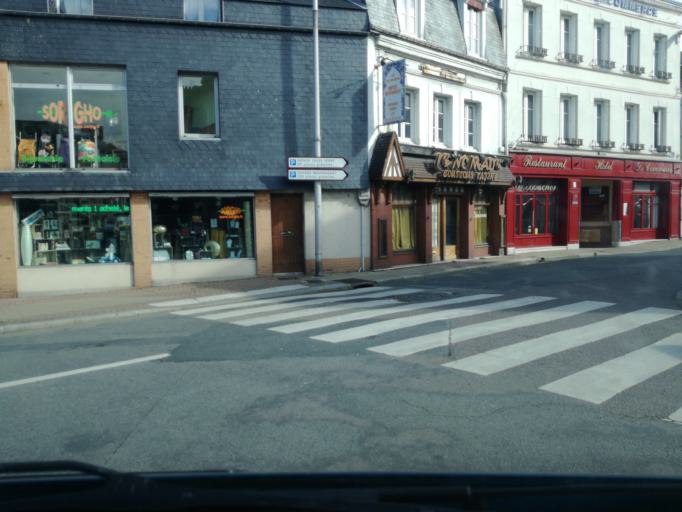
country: FR
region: Haute-Normandie
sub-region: Departement de la Seine-Maritime
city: Fecamp
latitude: 49.7582
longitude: 0.3769
